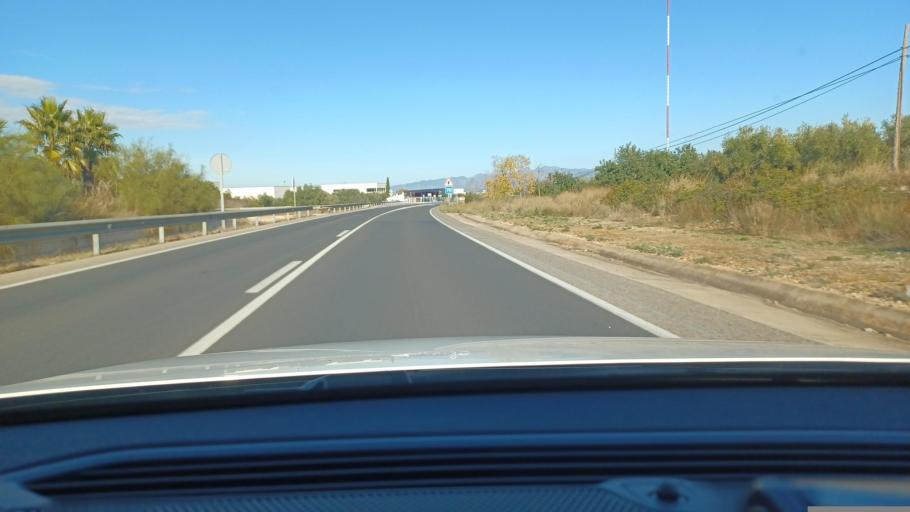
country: ES
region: Catalonia
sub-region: Provincia de Tarragona
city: Santa Barbara
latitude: 40.7343
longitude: 0.5031
